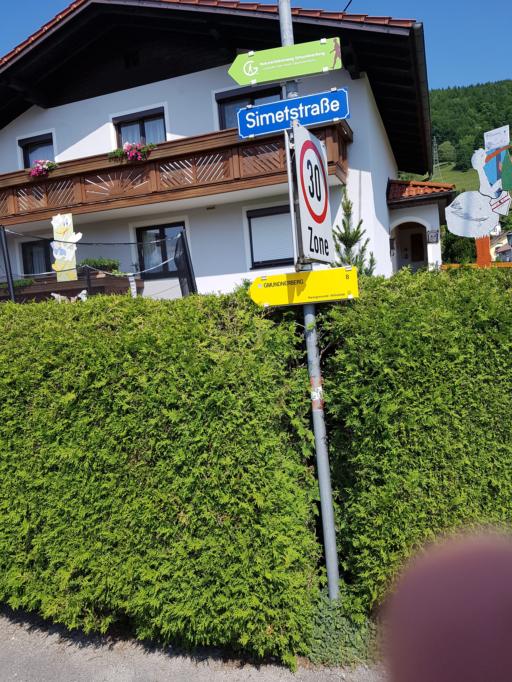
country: AT
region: Upper Austria
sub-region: Politischer Bezirk Gmunden
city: Altmunster
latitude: 47.9120
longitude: 13.7660
